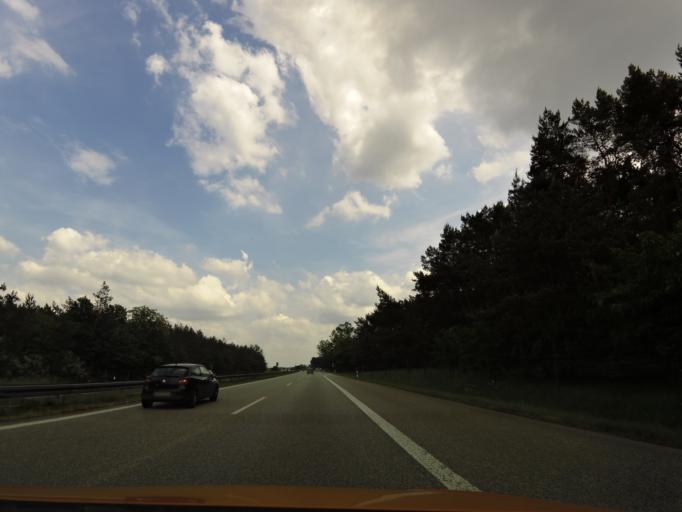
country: DE
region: Mecklenburg-Vorpommern
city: Neustadt-Glewe
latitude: 53.3717
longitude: 11.6451
